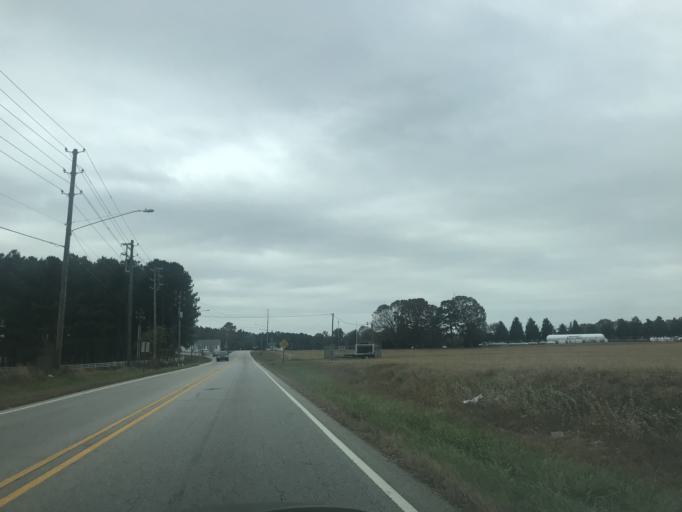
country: US
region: North Carolina
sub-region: Franklin County
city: Youngsville
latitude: 36.0315
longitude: -78.4824
